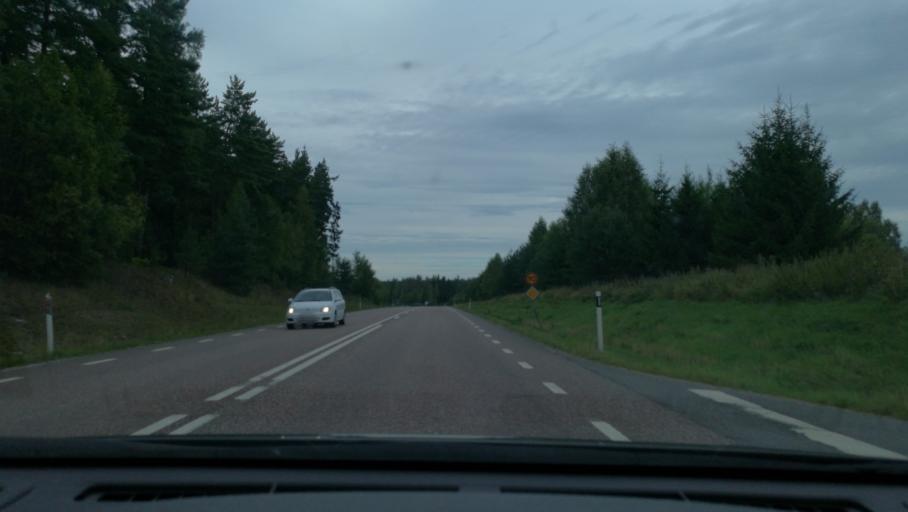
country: SE
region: Soedermanland
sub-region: Katrineholms Kommun
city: Katrineholm
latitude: 59.0410
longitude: 16.2183
